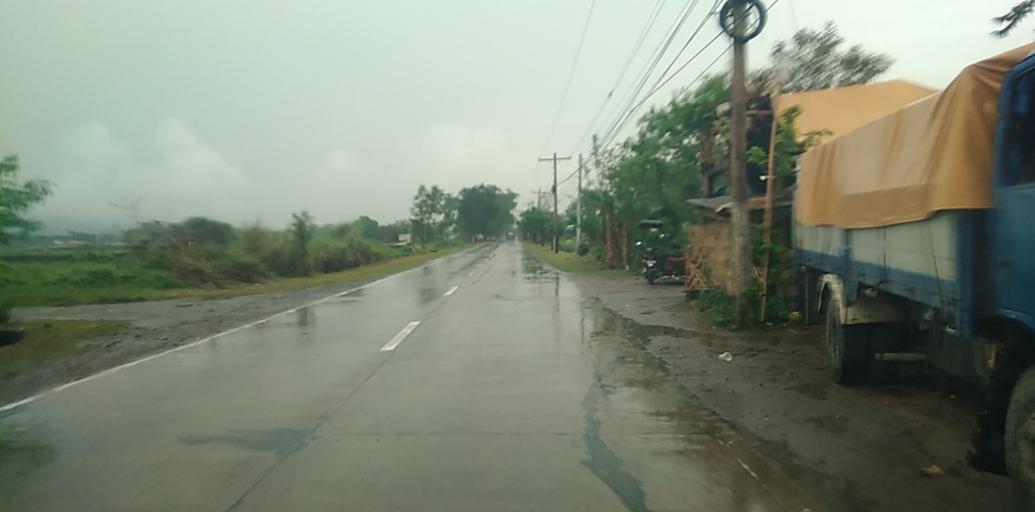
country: PH
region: Central Luzon
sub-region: Province of Pampanga
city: San Antonio
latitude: 15.1587
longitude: 120.6972
